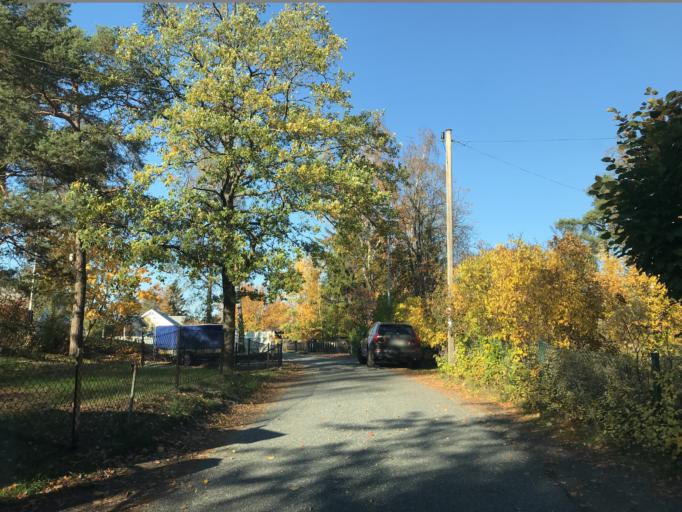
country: SE
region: Stockholm
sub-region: Sollentuna Kommun
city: Sollentuna
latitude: 59.4215
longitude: 17.9354
